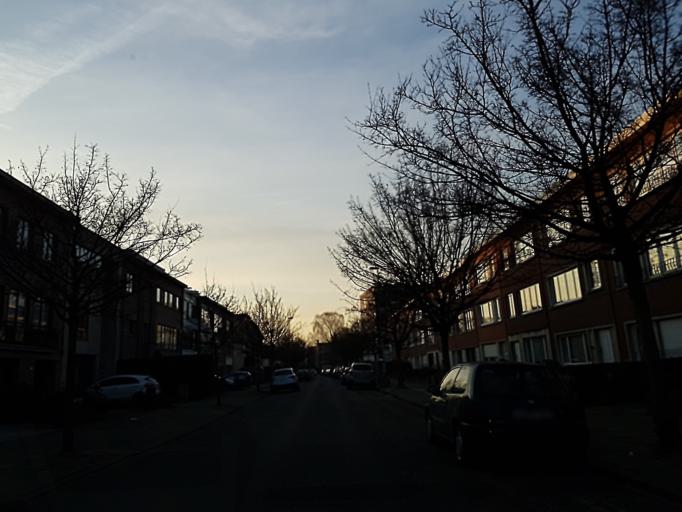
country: BE
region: Flanders
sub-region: Provincie Antwerpen
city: Edegem
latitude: 51.1766
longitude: 4.4231
